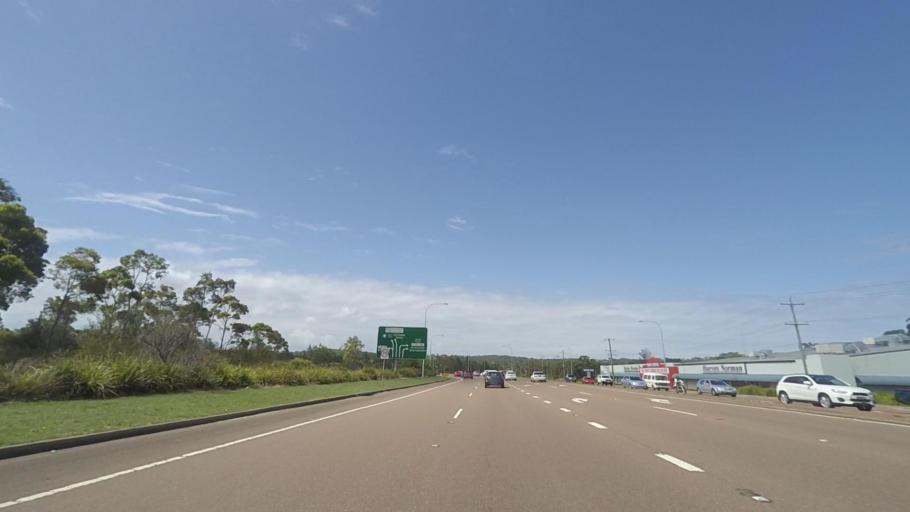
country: AU
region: New South Wales
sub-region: Lake Macquarie Shire
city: Windale
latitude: -32.9944
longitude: 151.6879
